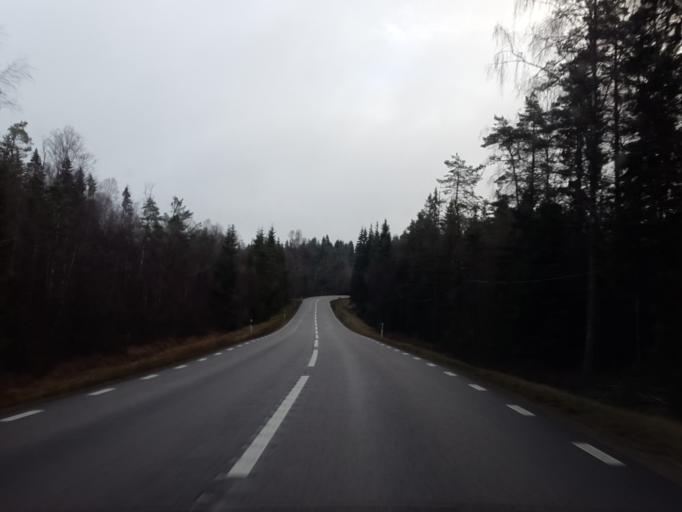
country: SE
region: Vaestra Goetaland
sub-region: Alingsas Kommun
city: Alingsas
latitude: 57.8419
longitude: 12.6685
